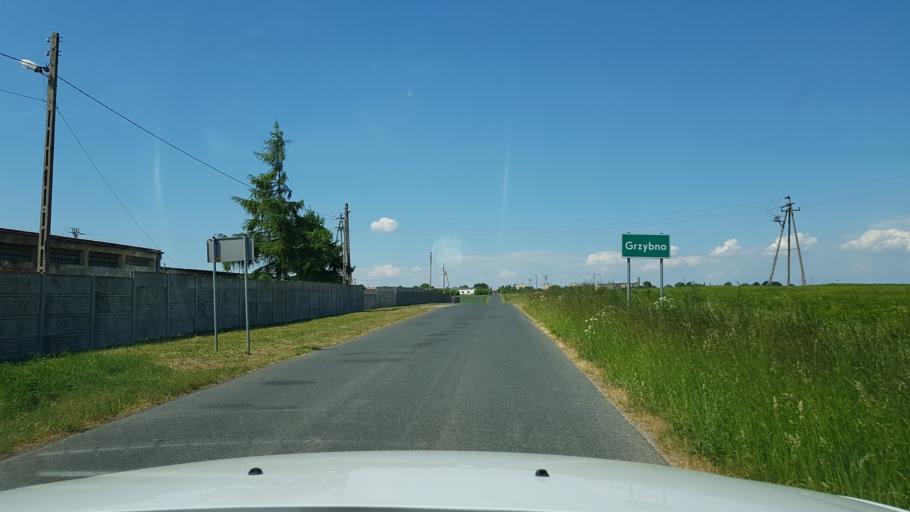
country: PL
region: West Pomeranian Voivodeship
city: Trzcinsko Zdroj
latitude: 53.0103
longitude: 14.5648
